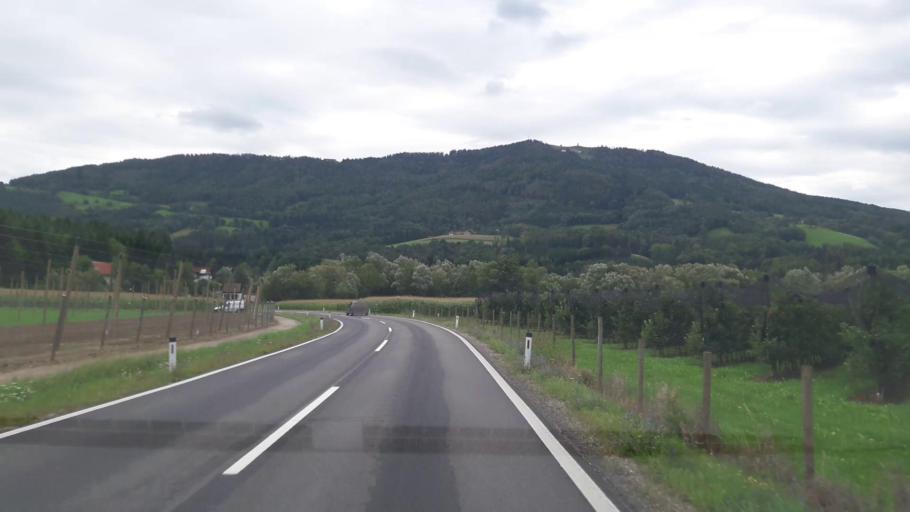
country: AT
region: Styria
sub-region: Politischer Bezirk Weiz
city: Floing
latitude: 47.2438
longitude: 15.7355
